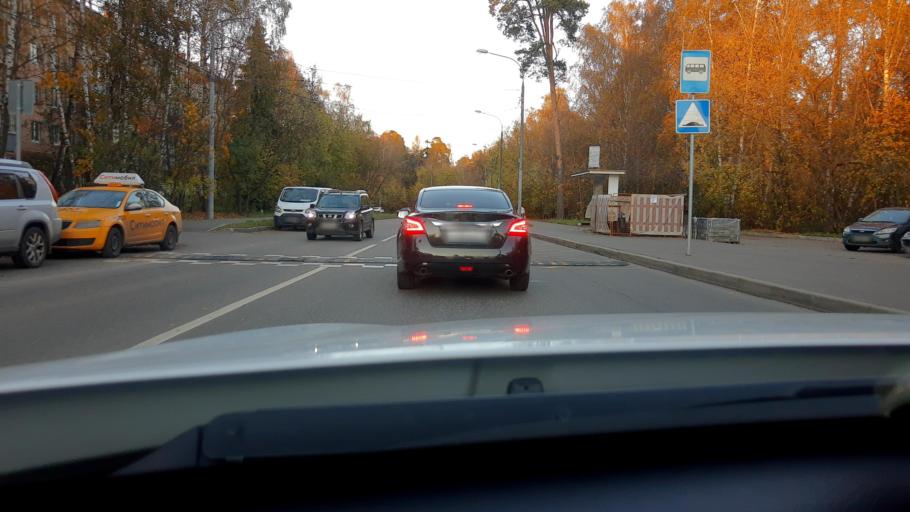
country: RU
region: Moscow
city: Rublevo
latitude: 55.7821
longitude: 37.3590
